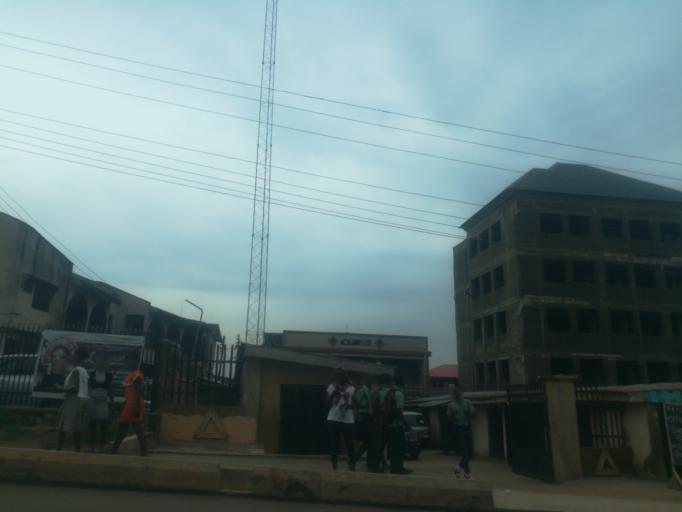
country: NG
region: Oyo
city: Ibadan
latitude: 7.3957
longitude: 3.9241
